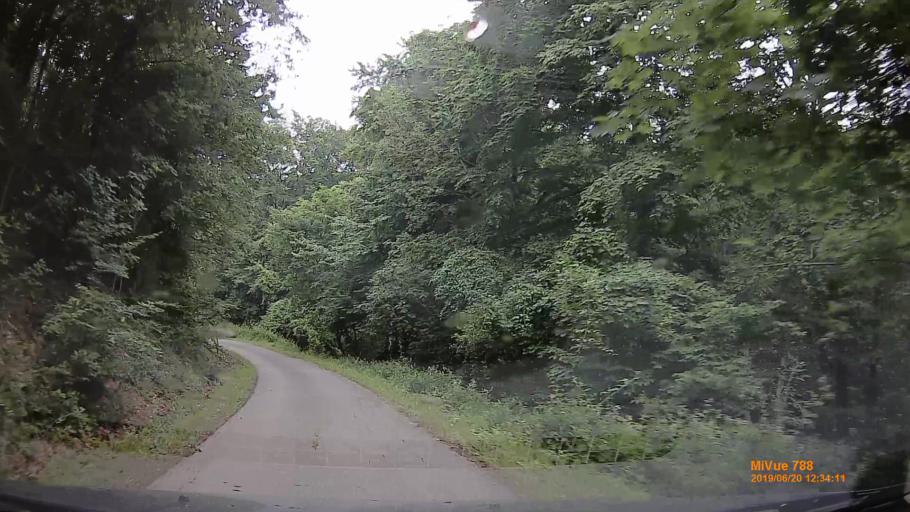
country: HU
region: Baranya
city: Hosszuheteny
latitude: 46.1945
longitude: 18.3683
